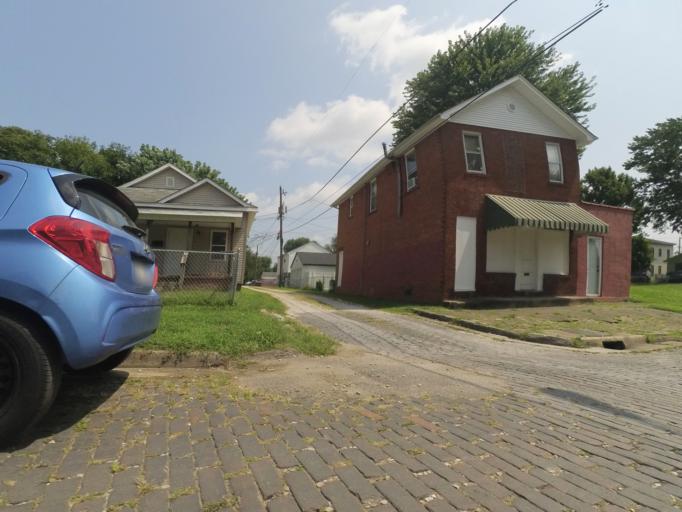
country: US
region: West Virginia
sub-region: Cabell County
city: Huntington
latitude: 38.4340
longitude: -82.4056
